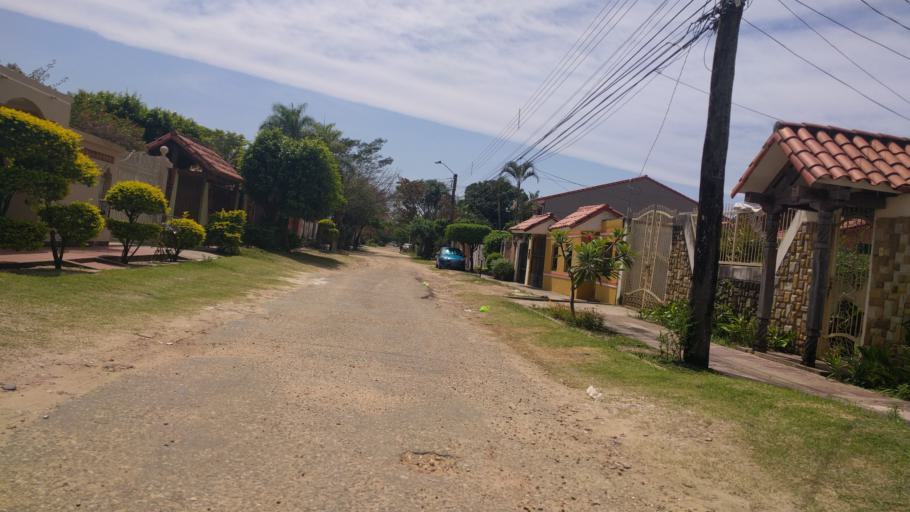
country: BO
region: Santa Cruz
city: Santa Cruz de la Sierra
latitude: -17.8176
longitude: -63.2237
